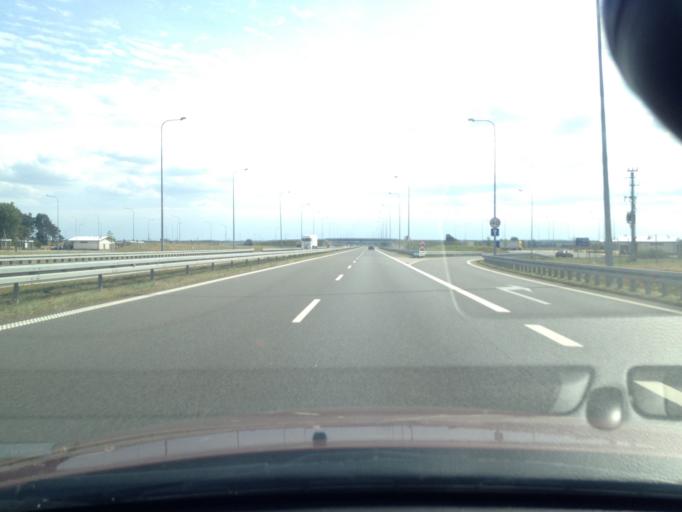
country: PL
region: West Pomeranian Voivodeship
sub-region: Powiat pyrzycki
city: Bielice
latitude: 53.1543
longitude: 14.7112
